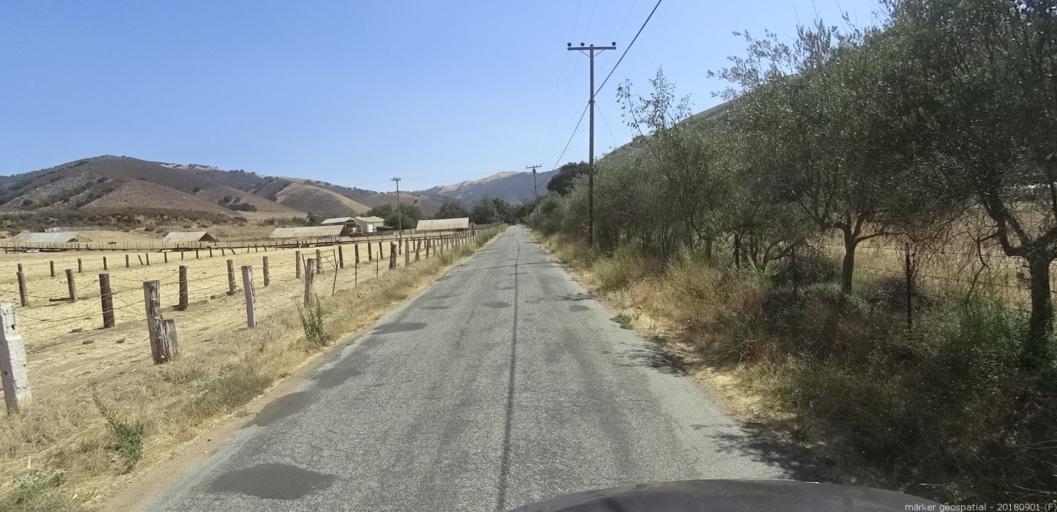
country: US
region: California
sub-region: Monterey County
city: Chualar
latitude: 36.6032
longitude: -121.4303
